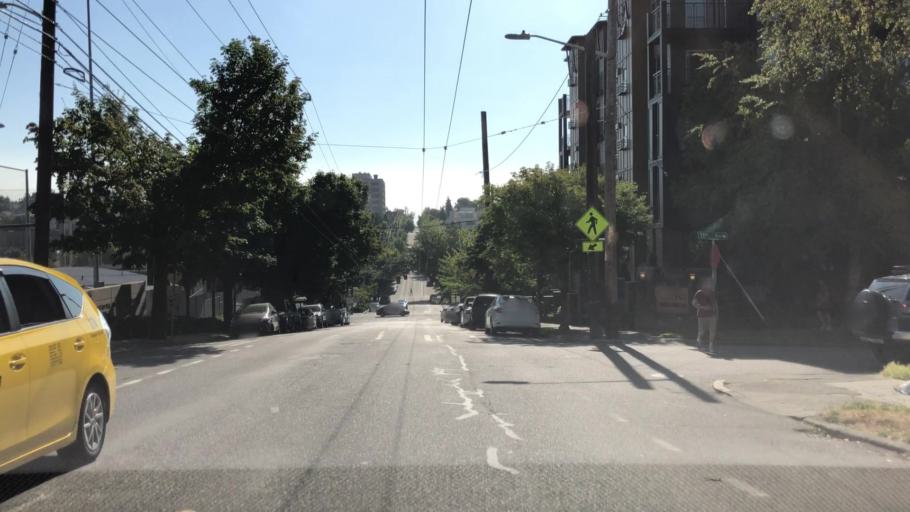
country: US
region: Washington
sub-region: King County
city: Seattle
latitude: 47.6062
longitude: -122.3184
